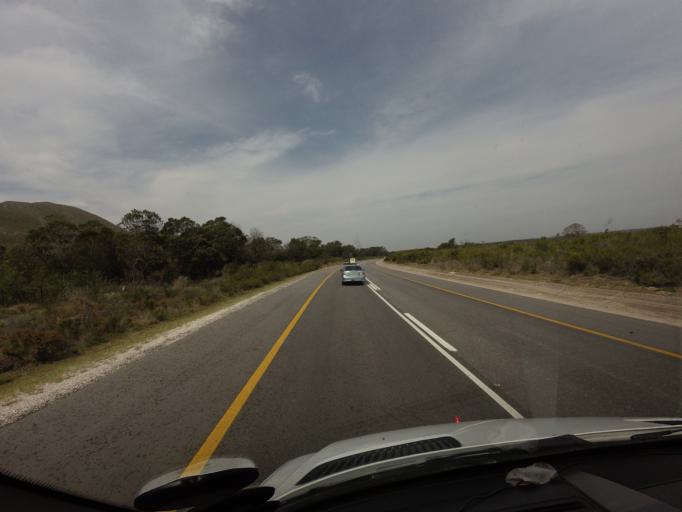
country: ZA
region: Eastern Cape
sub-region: Cacadu District Municipality
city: Kruisfontein
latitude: -33.9940
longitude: 24.7323
